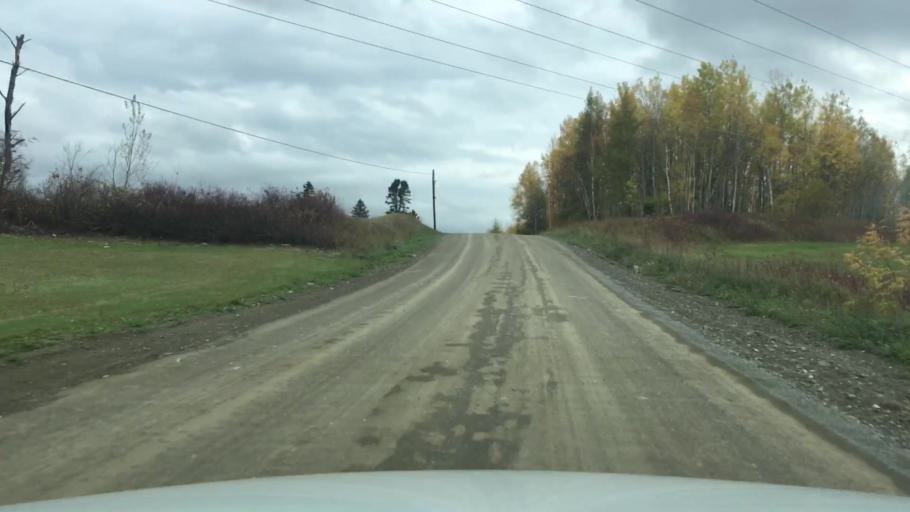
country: US
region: Maine
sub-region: Aroostook County
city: Easton
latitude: 46.5173
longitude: -67.8846
